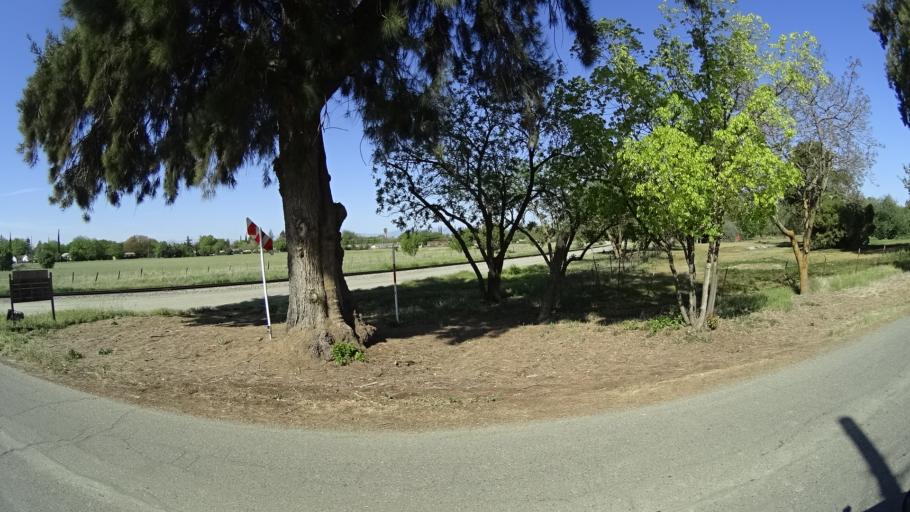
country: US
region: California
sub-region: Glenn County
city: Willows
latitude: 39.5302
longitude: -122.1951
